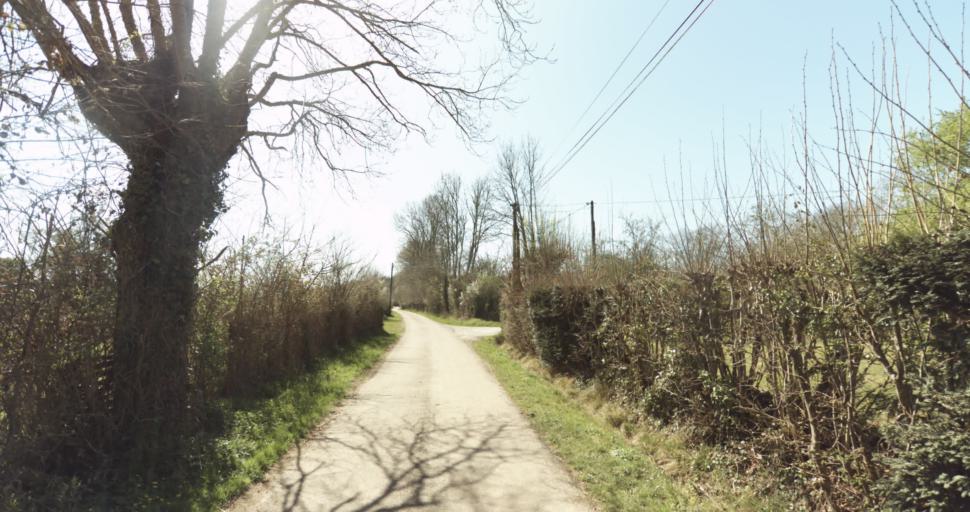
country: FR
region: Lower Normandy
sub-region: Departement du Calvados
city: Saint-Pierre-sur-Dives
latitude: 48.9940
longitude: 0.0568
